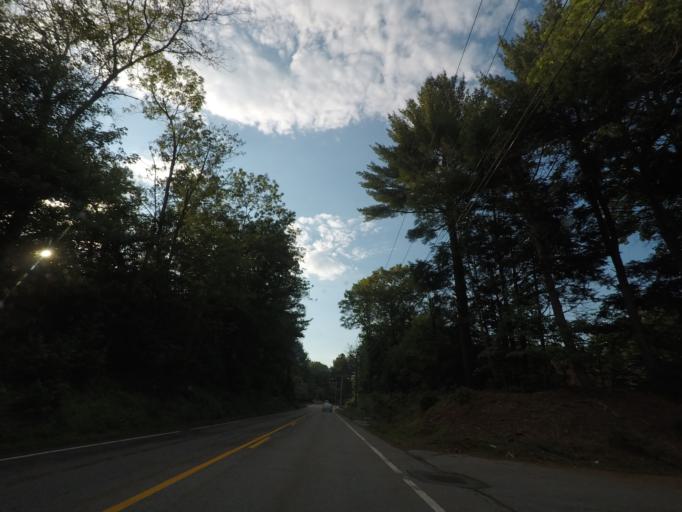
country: US
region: Connecticut
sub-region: Windham County
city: Quinebaug
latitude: 42.0321
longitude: -71.9652
